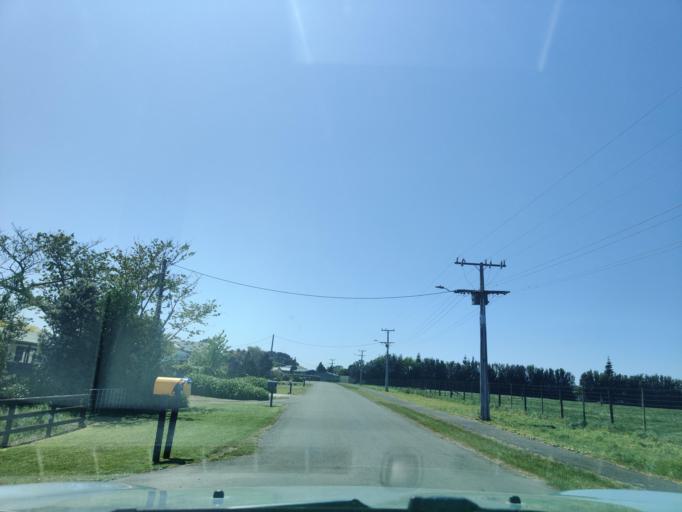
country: NZ
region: Taranaki
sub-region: South Taranaki District
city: Hawera
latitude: -39.5943
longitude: 174.2687
